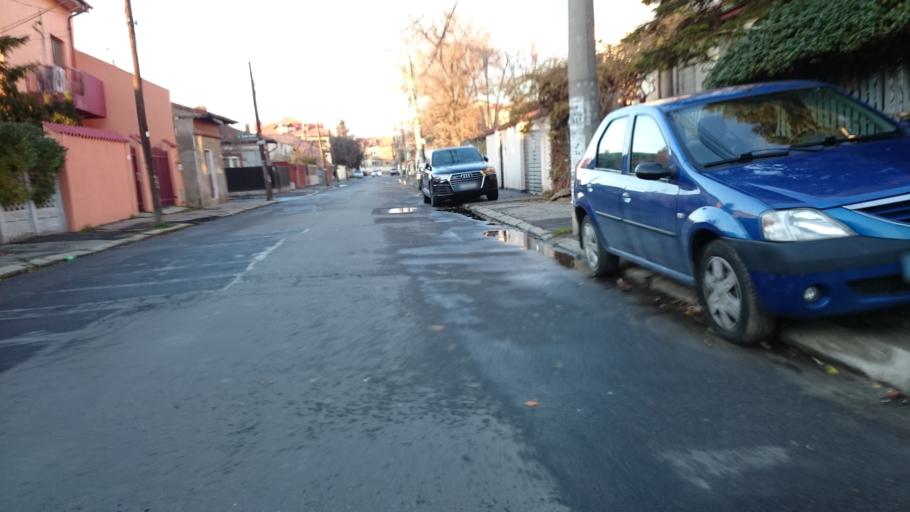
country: RO
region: Bucuresti
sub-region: Municipiul Bucuresti
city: Bucuresti
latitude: 44.4192
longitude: 26.0582
